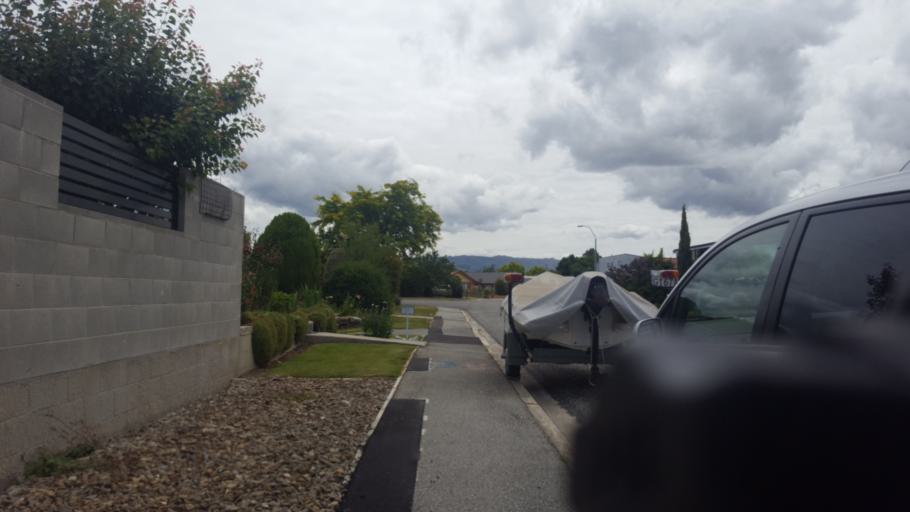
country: NZ
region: Otago
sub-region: Queenstown-Lakes District
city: Wanaka
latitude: -45.2551
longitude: 169.3868
